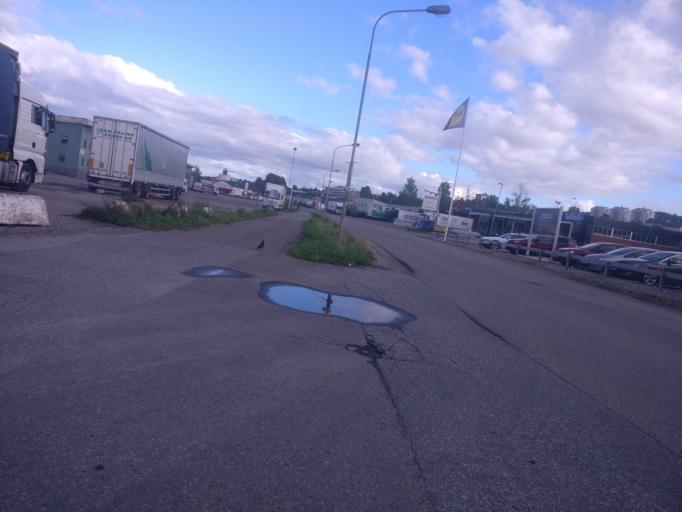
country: SE
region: Vaesternorrland
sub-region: Sundsvalls Kommun
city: Sundsvall
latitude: 62.3873
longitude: 17.3226
